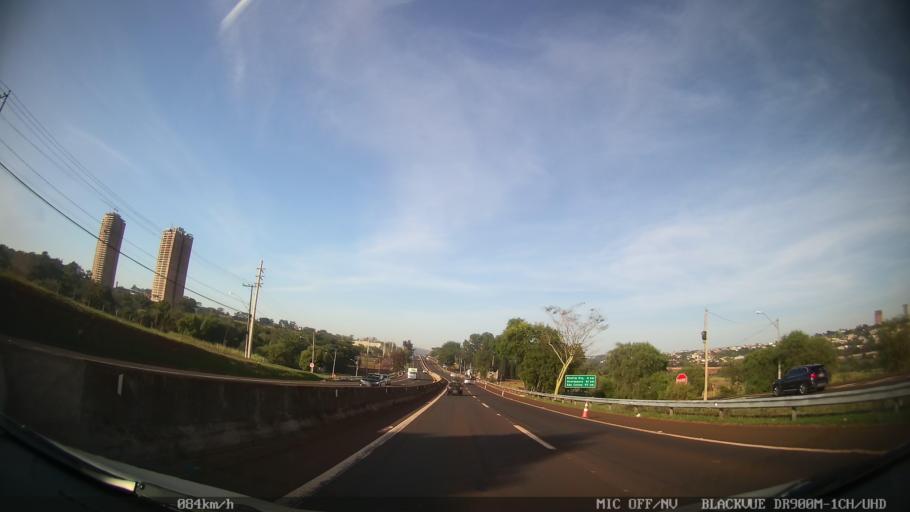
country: BR
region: Sao Paulo
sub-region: Ribeirao Preto
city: Ribeirao Preto
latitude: -21.2344
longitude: -47.8187
